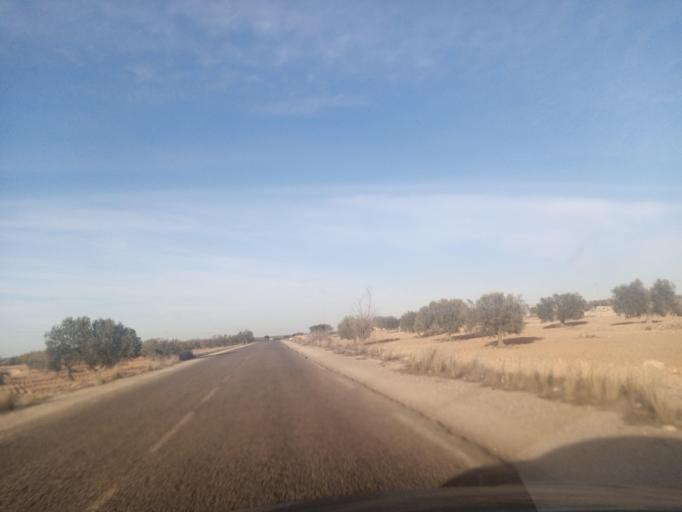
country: TN
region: Al Mahdiyah
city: Shurban
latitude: 34.9520
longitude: 10.3570
